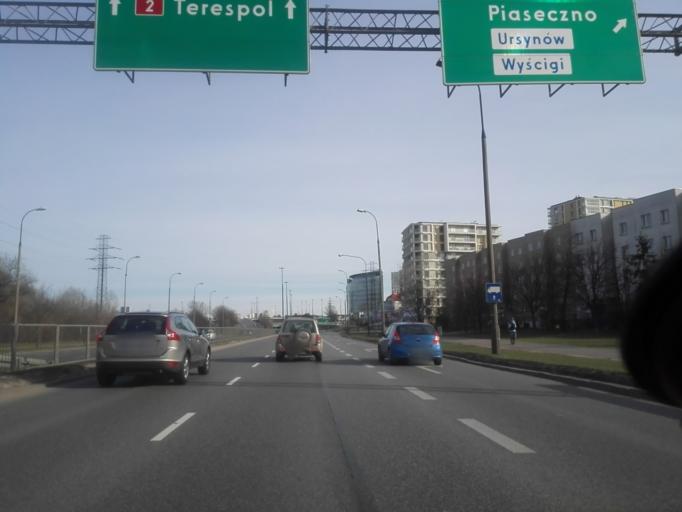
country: PL
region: Masovian Voivodeship
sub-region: Warszawa
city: Mokotow
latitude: 52.1694
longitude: 21.0100
